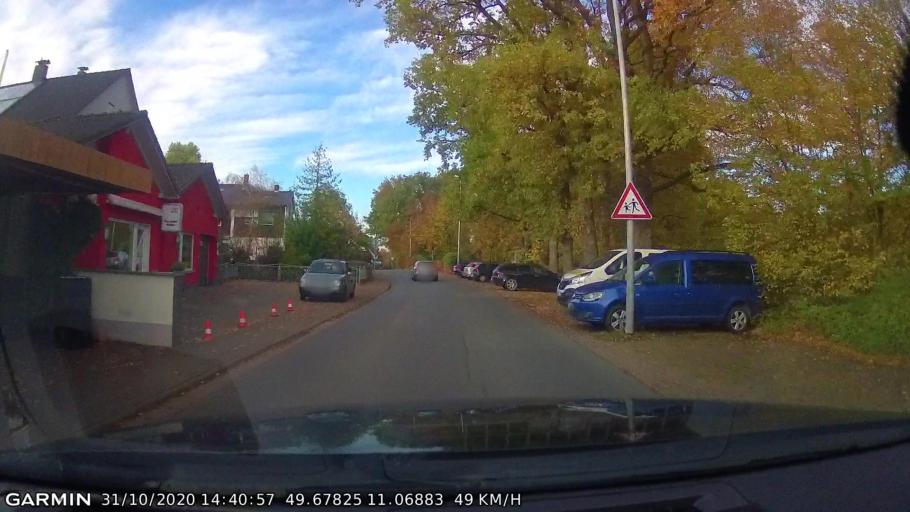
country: DE
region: Bavaria
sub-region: Upper Franconia
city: Poxdorf
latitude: 49.6783
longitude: 11.0688
